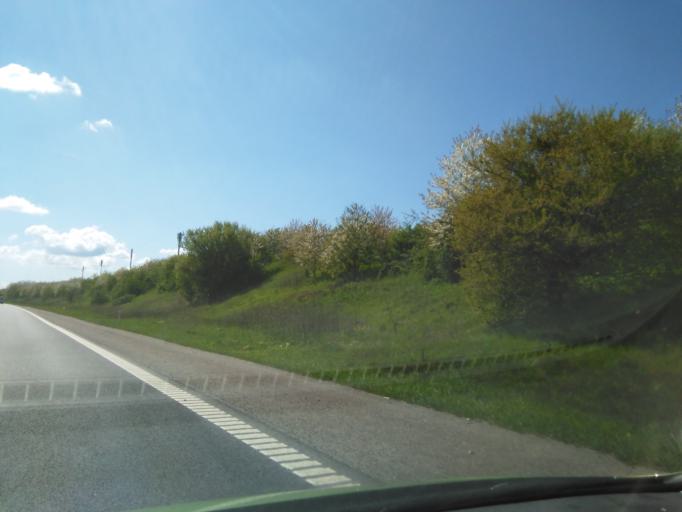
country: DK
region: Capital Region
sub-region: Frederiksberg Kommune
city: Frederiksberg
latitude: 55.6314
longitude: 12.5417
